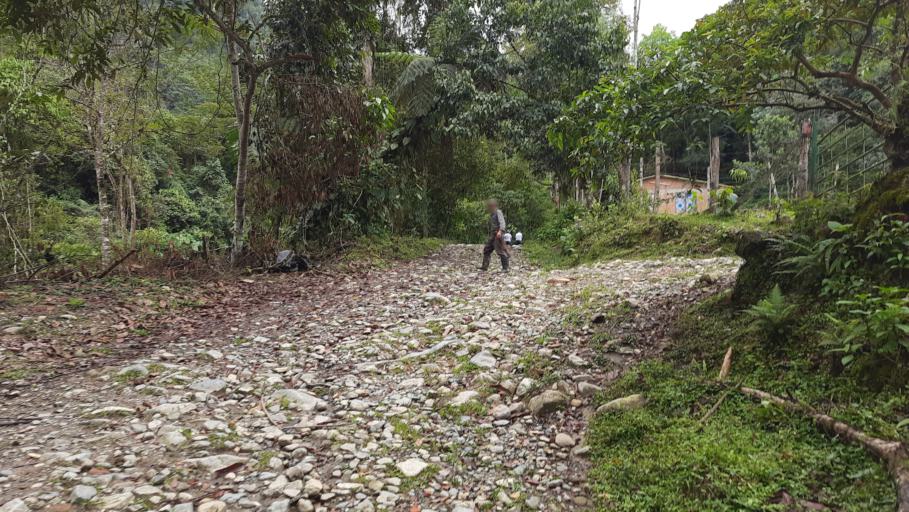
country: CO
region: Valle del Cauca
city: Buga
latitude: 3.8538
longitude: -76.1863
